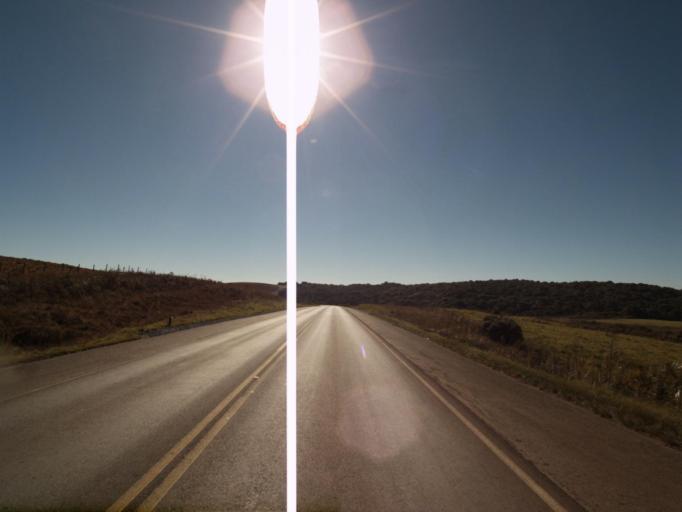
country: BR
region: Santa Catarina
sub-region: Joacaba
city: Joacaba
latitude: -26.7930
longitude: -51.6912
